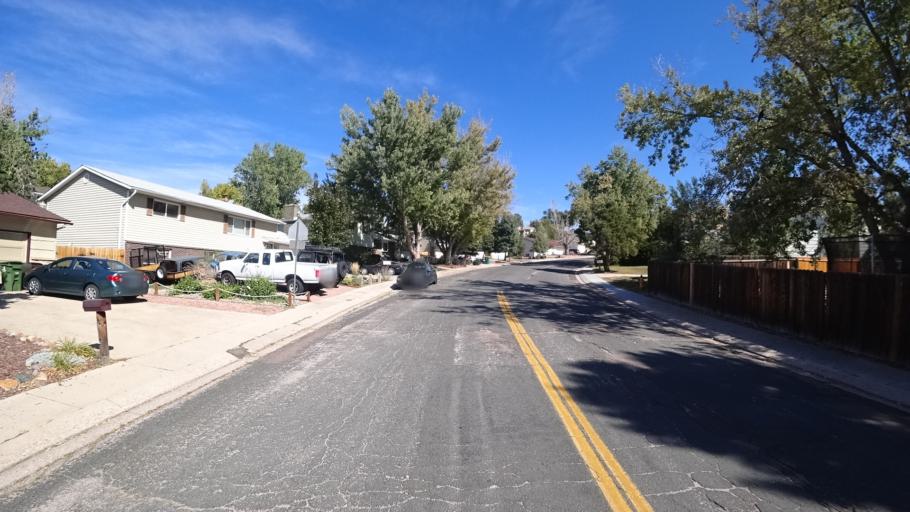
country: US
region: Colorado
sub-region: El Paso County
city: Cimarron Hills
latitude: 38.9094
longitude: -104.7714
